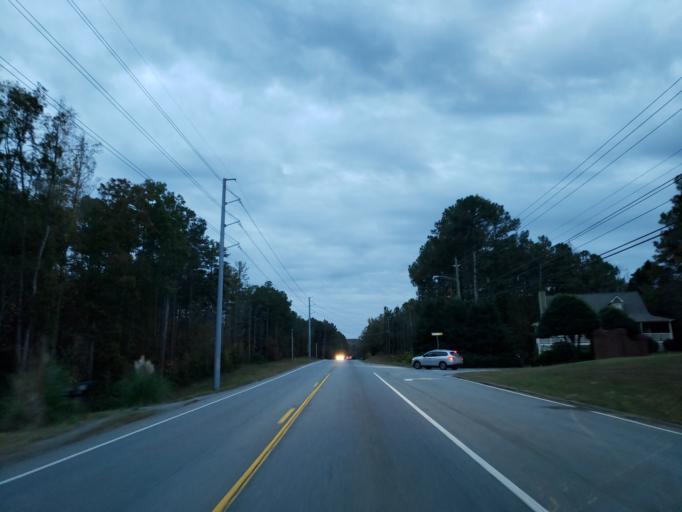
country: US
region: Georgia
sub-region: Paulding County
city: Hiram
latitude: 33.9618
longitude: -84.7395
